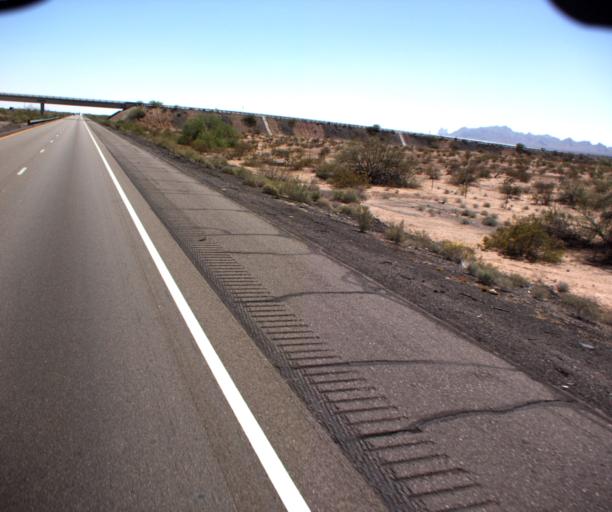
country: US
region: Arizona
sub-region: La Paz County
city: Salome
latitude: 33.5952
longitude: -113.5290
